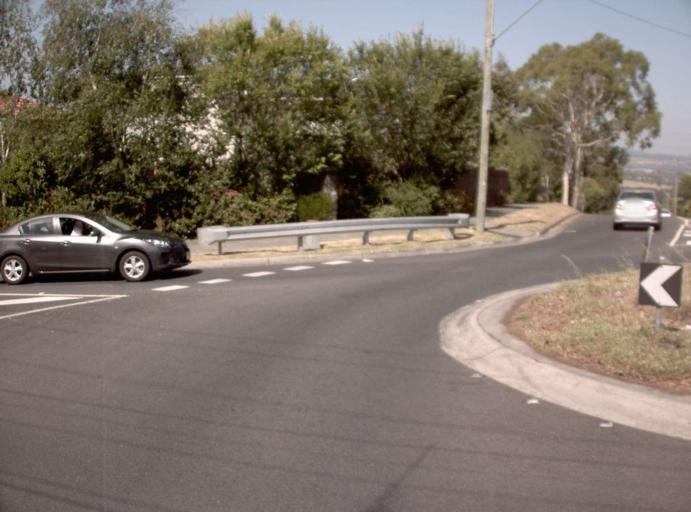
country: AU
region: Victoria
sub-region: Whitehorse
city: Vermont South
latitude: -37.8902
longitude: 145.1761
